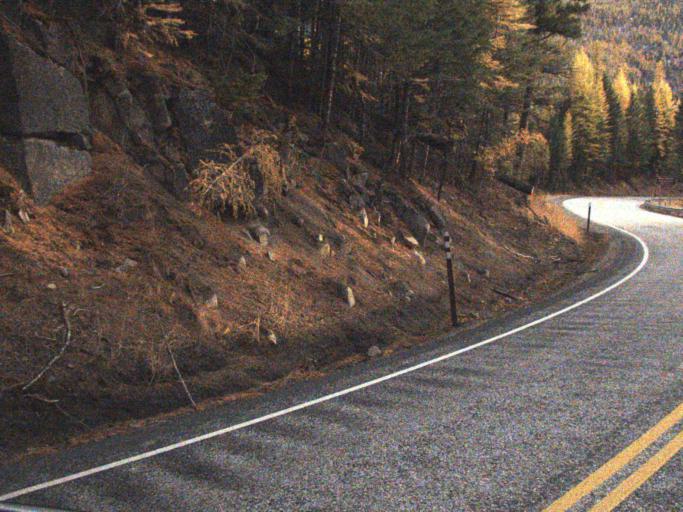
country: US
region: Washington
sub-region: Ferry County
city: Republic
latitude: 48.6024
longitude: -118.5135
